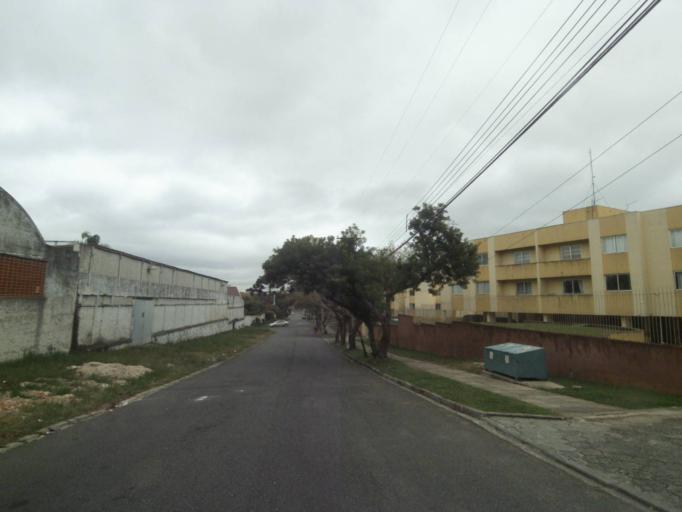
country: BR
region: Parana
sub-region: Curitiba
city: Curitiba
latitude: -25.4675
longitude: -49.2789
